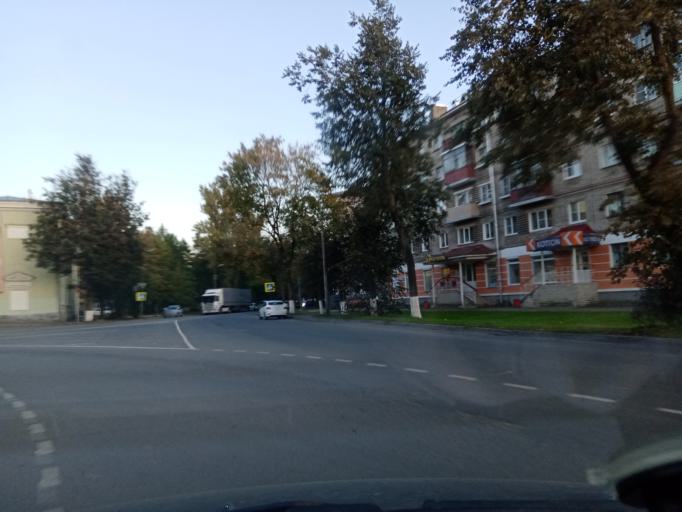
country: RU
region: Pskov
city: Pskov
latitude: 57.8075
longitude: 28.3396
